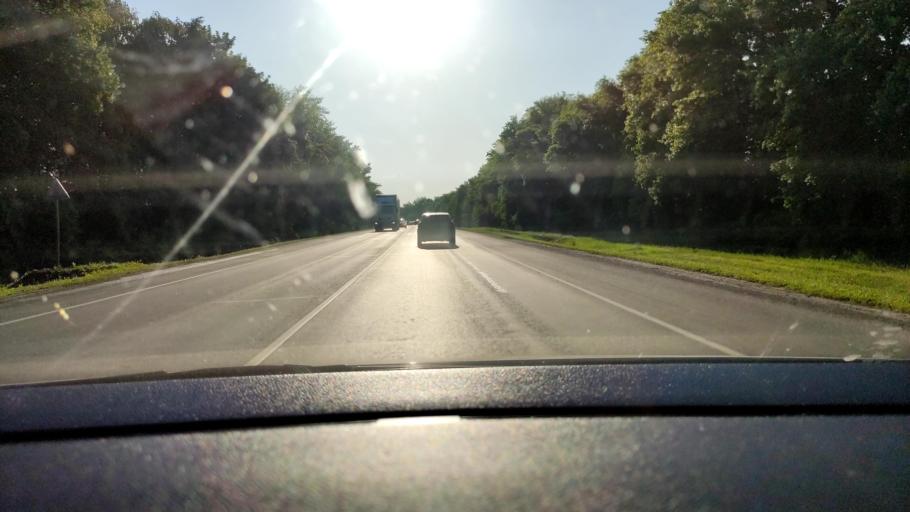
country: RU
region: Voronezj
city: Kashirskoye
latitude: 51.4904
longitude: 39.6269
